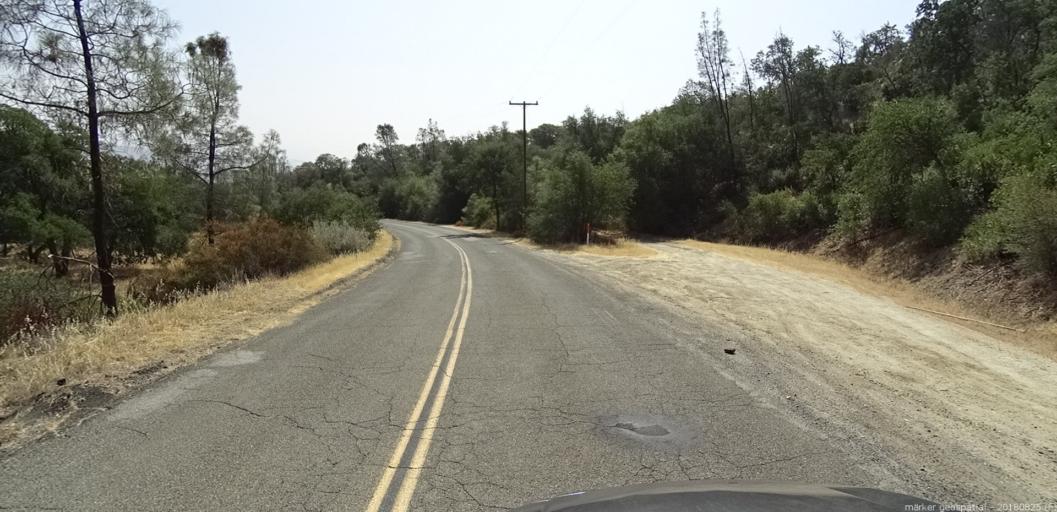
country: US
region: California
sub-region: San Luis Obispo County
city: San Miguel
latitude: 35.9206
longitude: -120.5312
